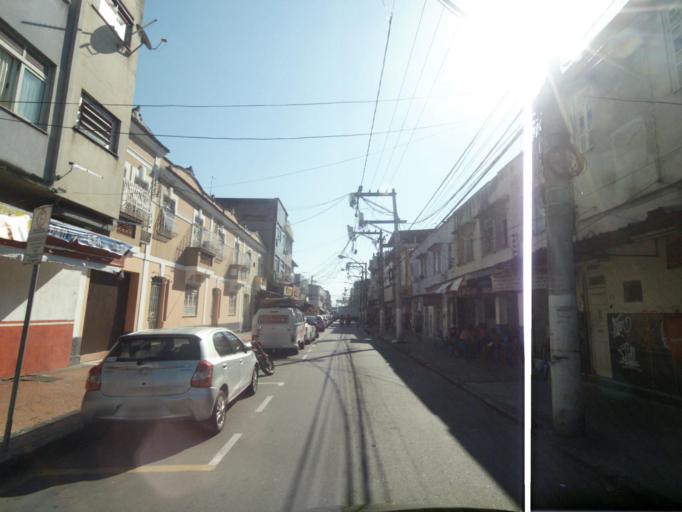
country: BR
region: Rio de Janeiro
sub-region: Niteroi
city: Niteroi
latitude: -22.8883
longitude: -43.1220
